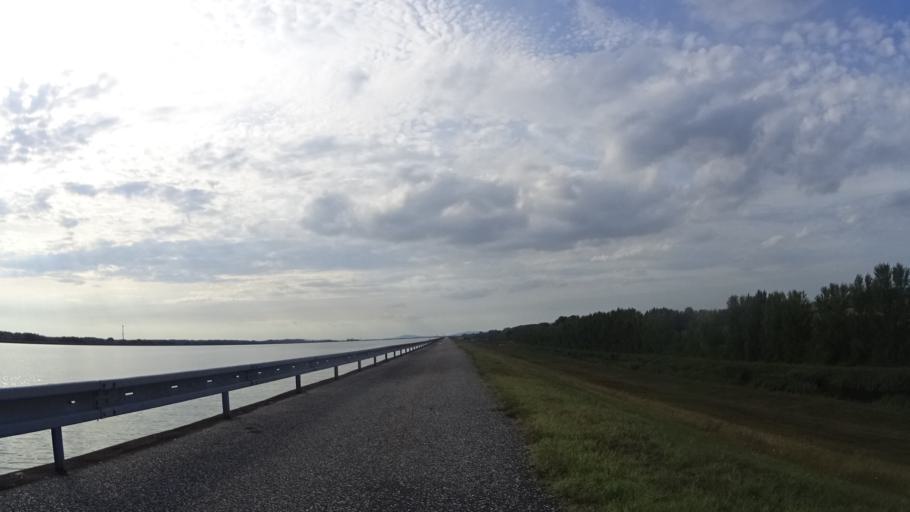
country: HU
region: Gyor-Moson-Sopron
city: Halaszi
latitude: 47.9593
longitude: 17.4257
